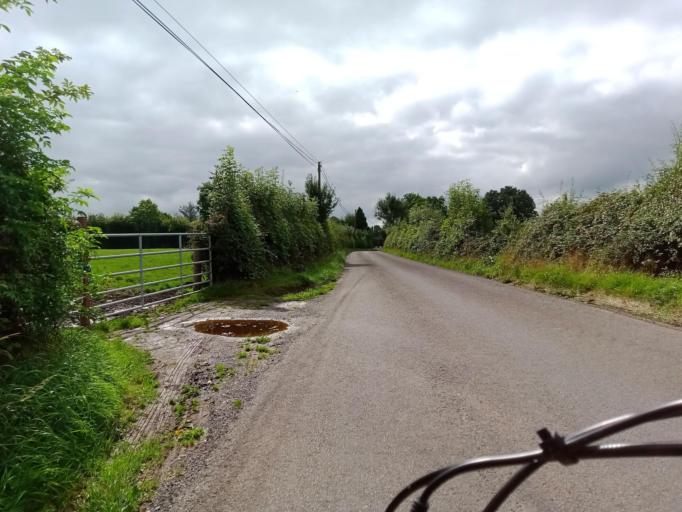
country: IE
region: Leinster
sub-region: Kilkenny
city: Callan
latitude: 52.5311
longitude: -7.2838
